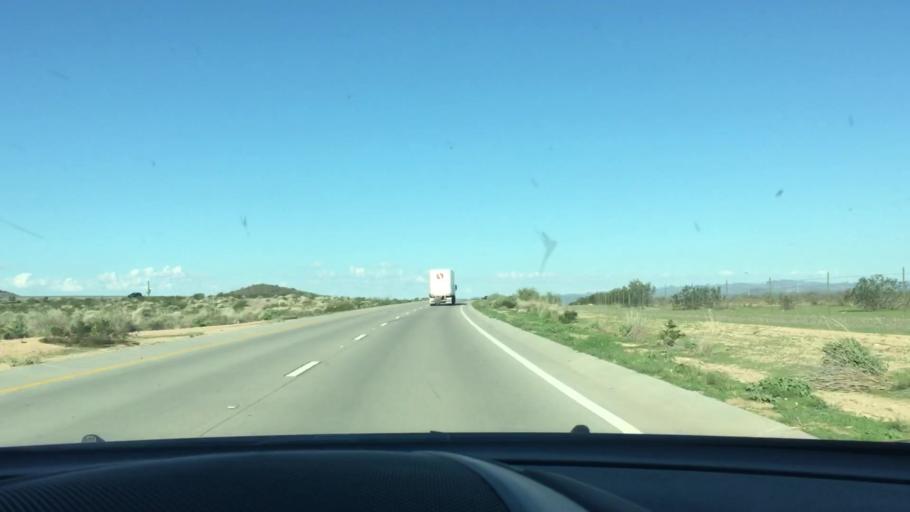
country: US
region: Arizona
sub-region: Maricopa County
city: Anthem
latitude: 33.7708
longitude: -112.1712
